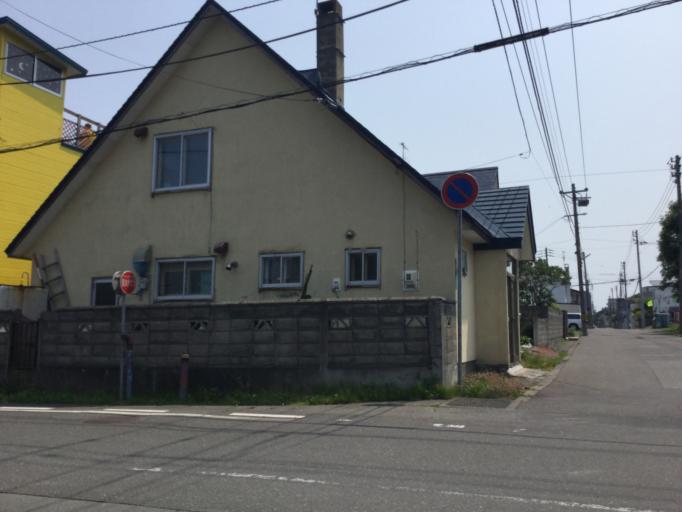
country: JP
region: Hokkaido
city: Wakkanai
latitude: 45.4010
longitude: 141.6764
